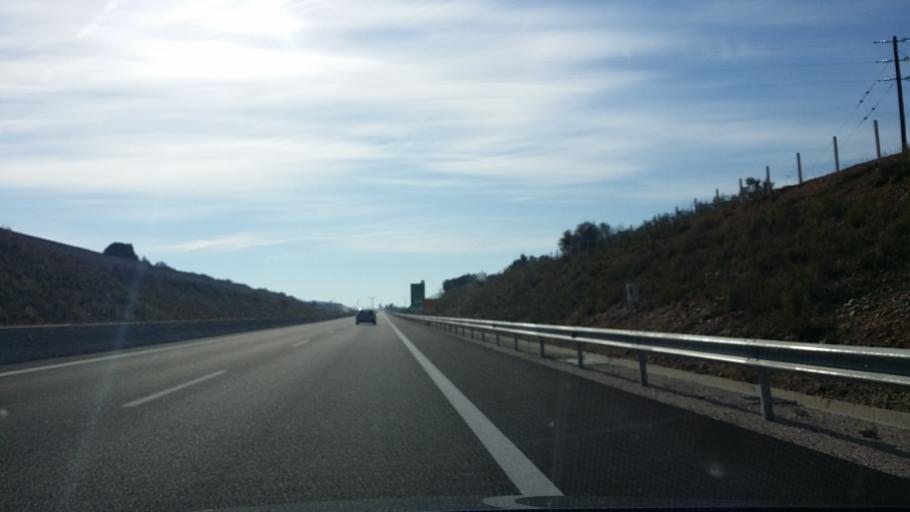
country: GR
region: West Greece
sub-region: Nomos Aitolias kai Akarnanias
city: Stanos
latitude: 38.7598
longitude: 21.2020
